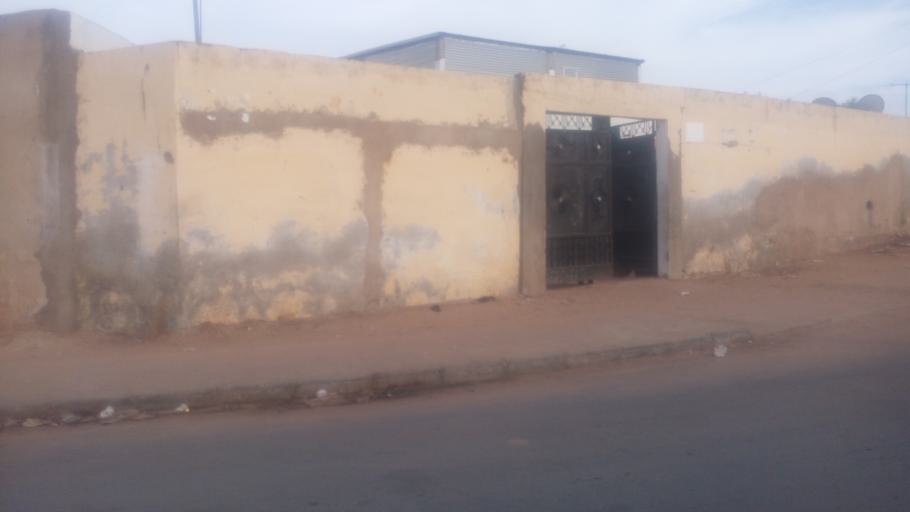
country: SN
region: Diourbel
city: Touba
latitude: 14.8656
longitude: -15.8740
